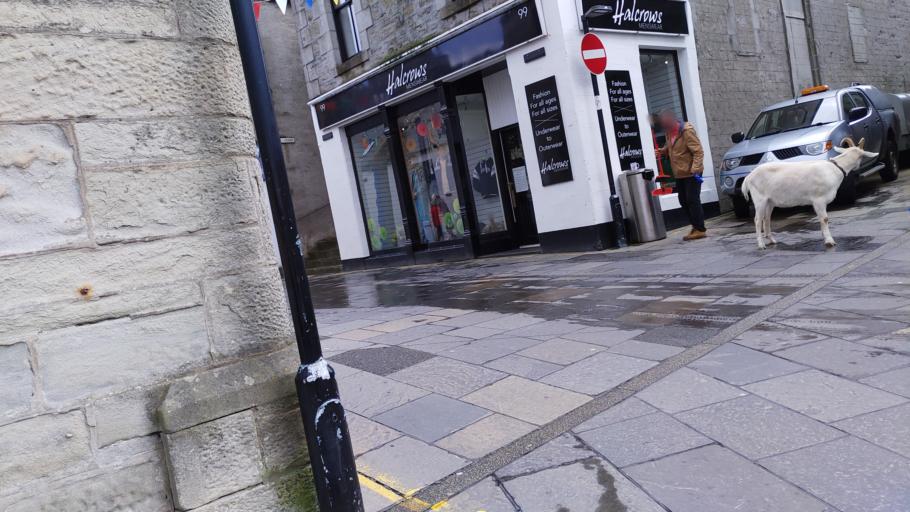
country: GB
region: Scotland
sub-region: Shetland Islands
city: Shetland
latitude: 60.1532
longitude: -1.1425
